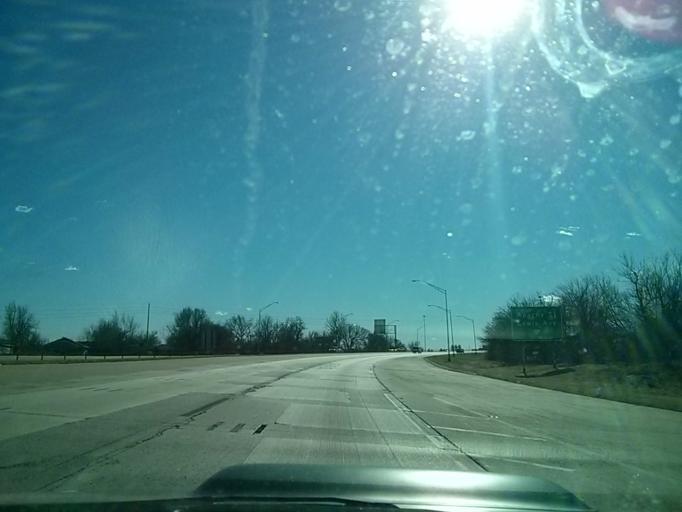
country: US
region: Oklahoma
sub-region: Tulsa County
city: Turley
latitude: 36.1957
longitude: -95.9520
